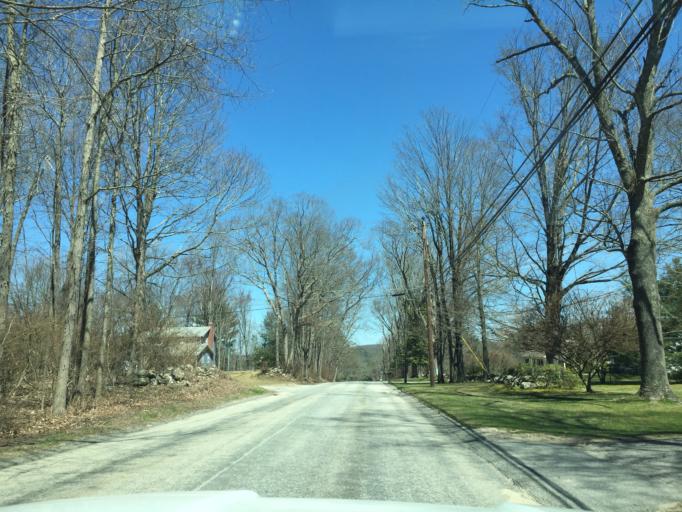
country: US
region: Connecticut
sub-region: Windham County
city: South Woodstock
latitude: 41.9571
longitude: -71.9721
